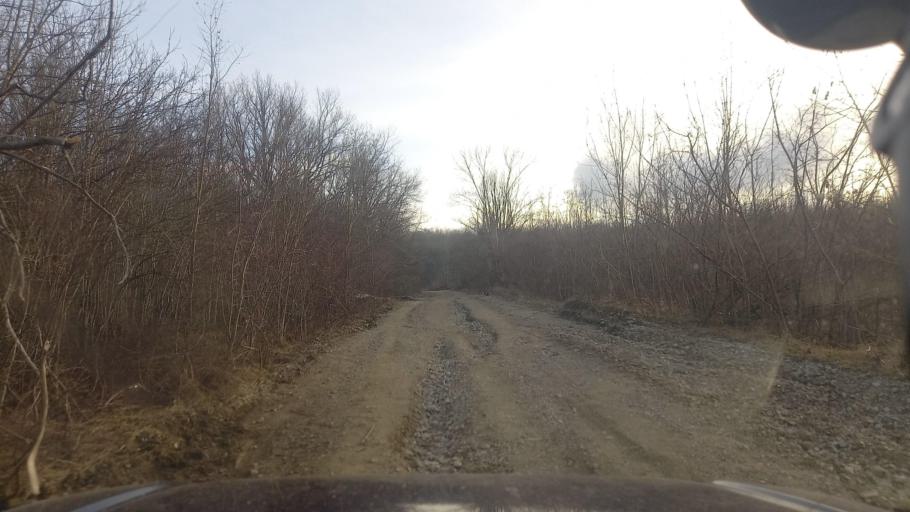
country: RU
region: Krasnodarskiy
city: Goryachiy Klyuch
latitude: 44.6913
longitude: 38.9781
